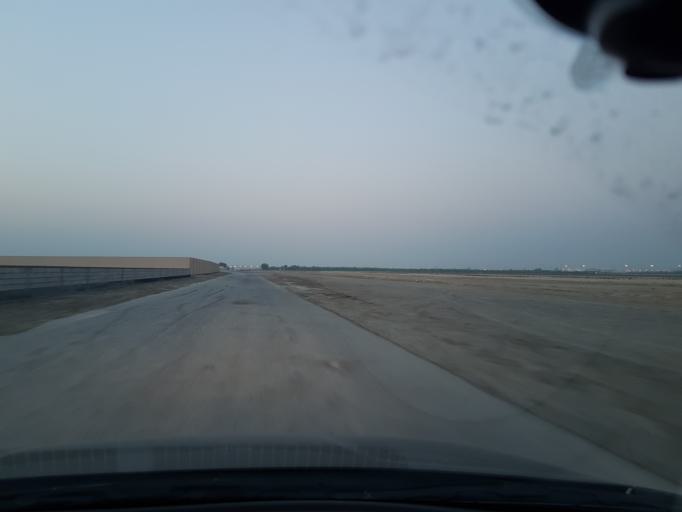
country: BH
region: Central Governorate
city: Dar Kulayb
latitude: 26.0045
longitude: 50.4742
